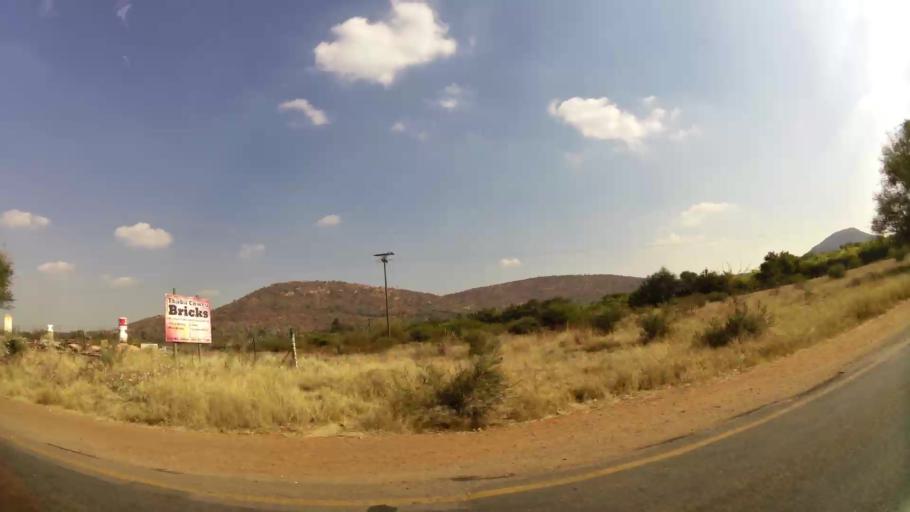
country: ZA
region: North-West
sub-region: Bojanala Platinum District Municipality
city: Rustenburg
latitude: -25.4975
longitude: 27.0887
